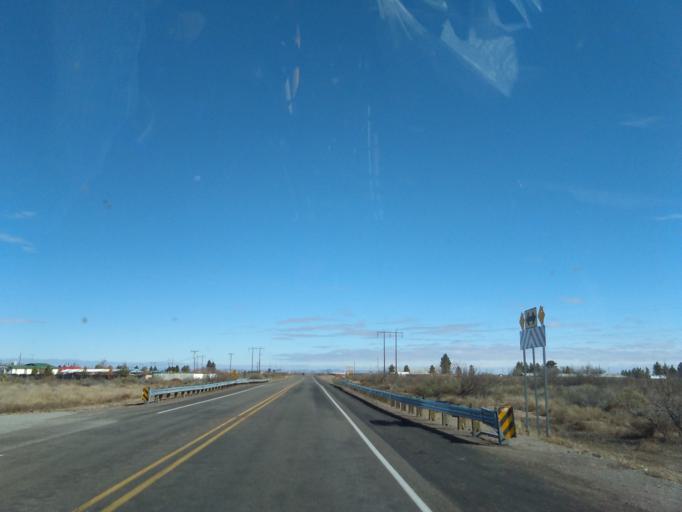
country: US
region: New Mexico
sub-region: Luna County
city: Deming
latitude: 32.2934
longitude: -107.7389
